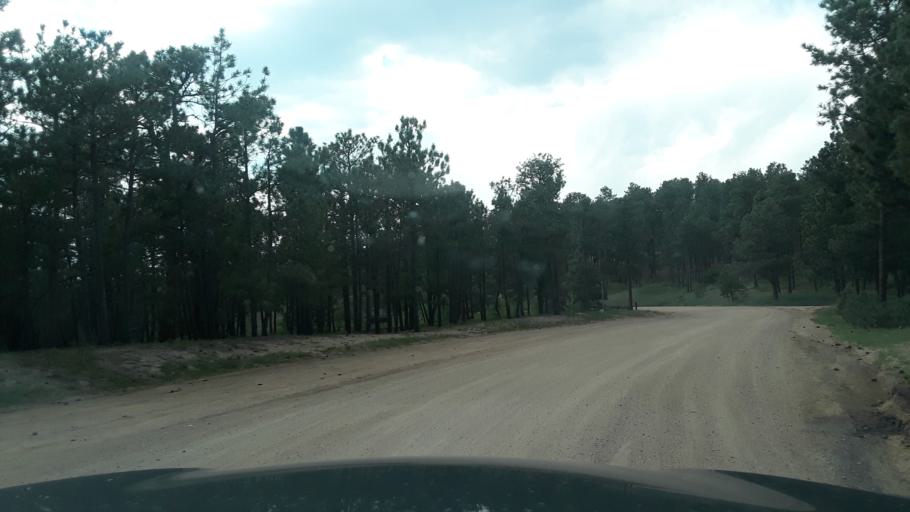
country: US
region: Colorado
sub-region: El Paso County
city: Gleneagle
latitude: 39.0604
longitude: -104.7902
